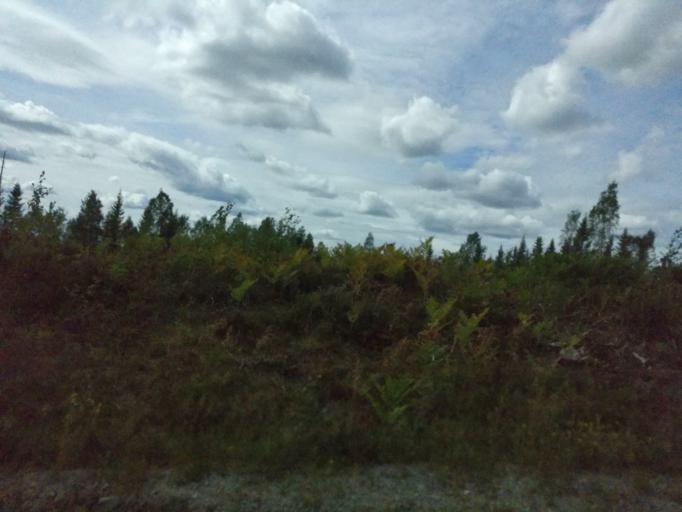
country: SE
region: Vaermland
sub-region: Hagfors Kommun
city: Hagfors
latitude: 60.0200
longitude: 13.7305
